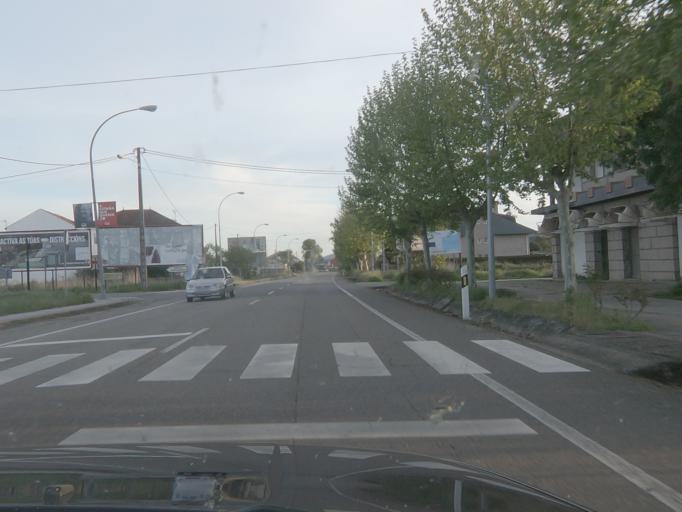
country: ES
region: Galicia
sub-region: Provincia de Ourense
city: Verin
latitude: 41.9265
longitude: -7.4419
